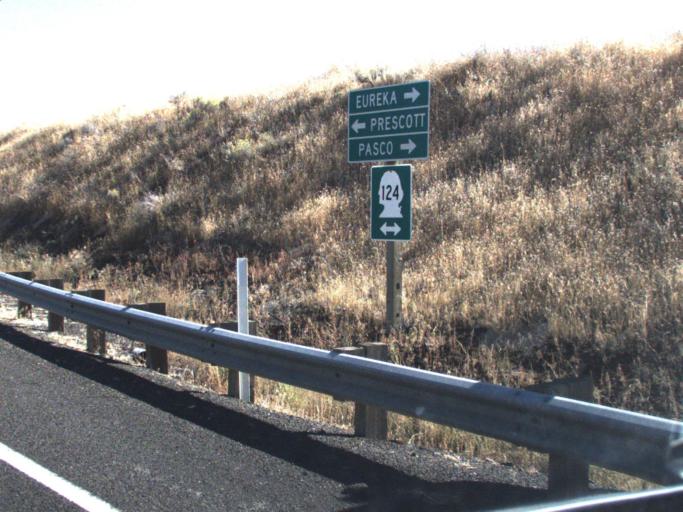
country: US
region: Washington
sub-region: Walla Walla County
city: Garrett
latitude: 46.2888
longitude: -118.4865
